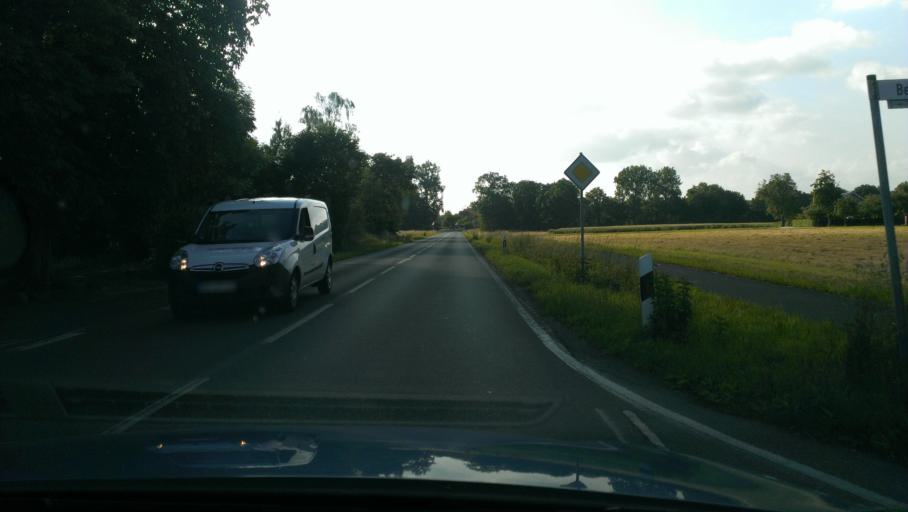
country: DE
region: North Rhine-Westphalia
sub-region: Regierungsbezirk Munster
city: Drensteinfurt
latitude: 51.8892
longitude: 7.7093
